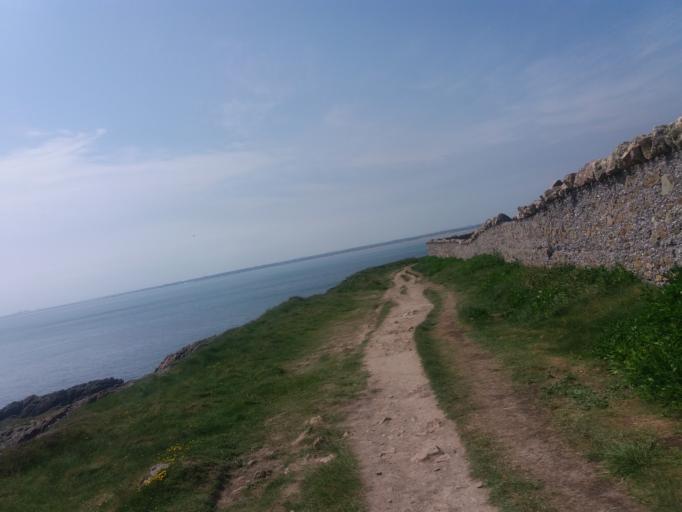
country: IE
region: Leinster
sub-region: Fingal County
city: Howth
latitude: 53.3629
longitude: -6.0842
